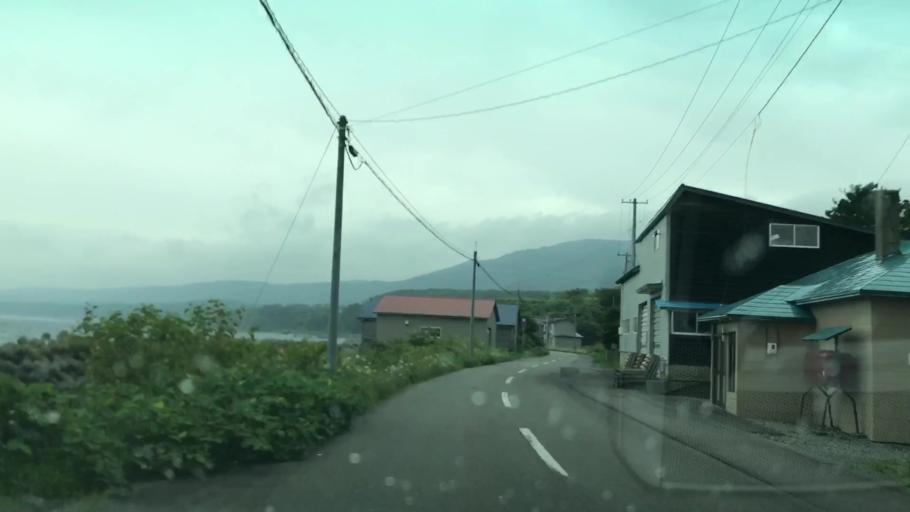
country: JP
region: Hokkaido
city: Iwanai
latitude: 42.7915
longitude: 140.2379
